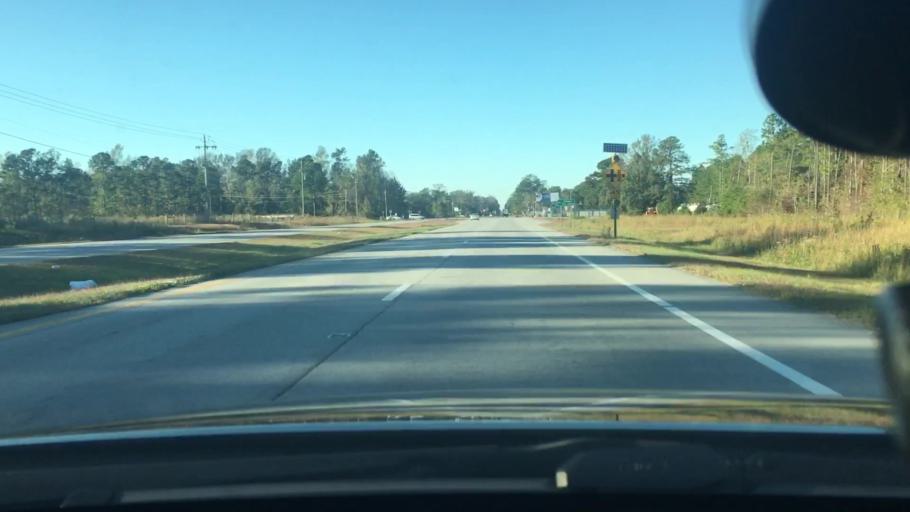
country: US
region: North Carolina
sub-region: Craven County
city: New Bern
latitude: 35.1507
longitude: -77.0339
